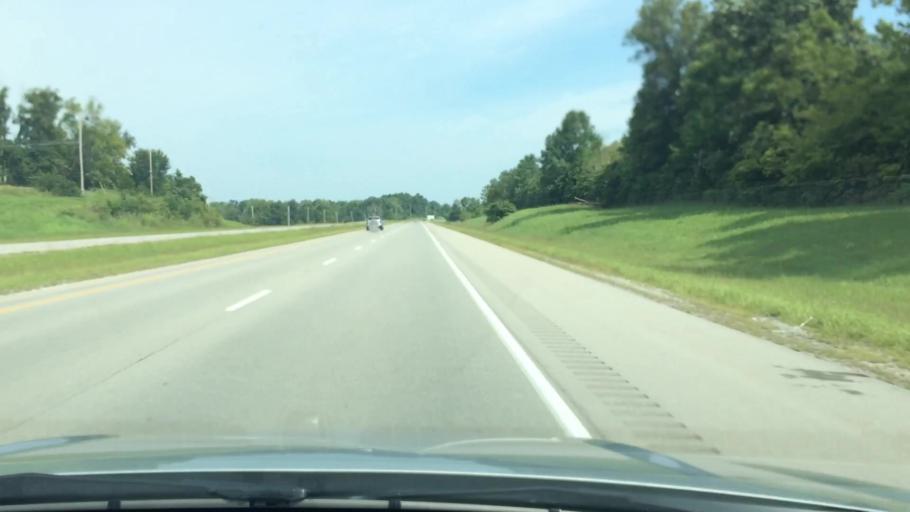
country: US
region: Kentucky
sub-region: Anderson County
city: Lawrenceburg
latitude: 38.1176
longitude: -84.9146
